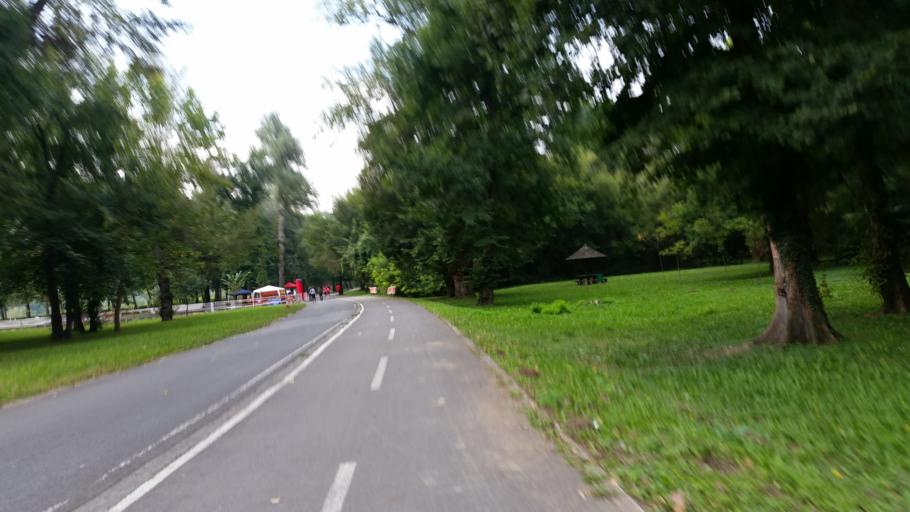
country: RS
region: Central Serbia
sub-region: Belgrade
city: Cukarica
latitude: 44.7803
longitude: 20.3747
